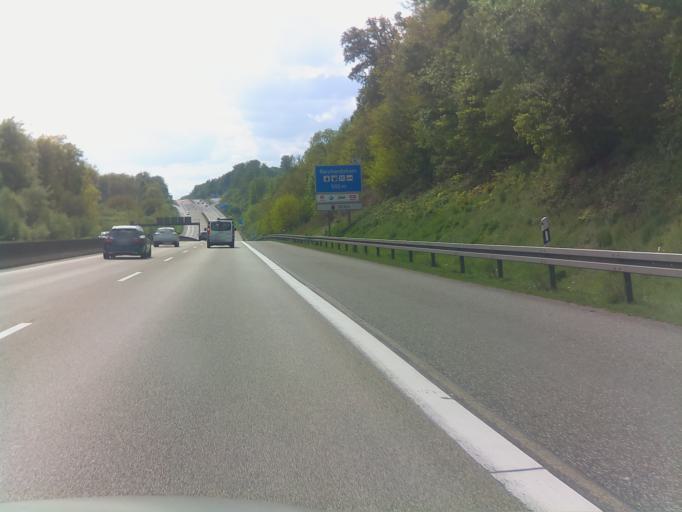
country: DE
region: Hesse
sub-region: Regierungsbezirk Giessen
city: Grunberg
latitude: 50.6283
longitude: 8.9096
